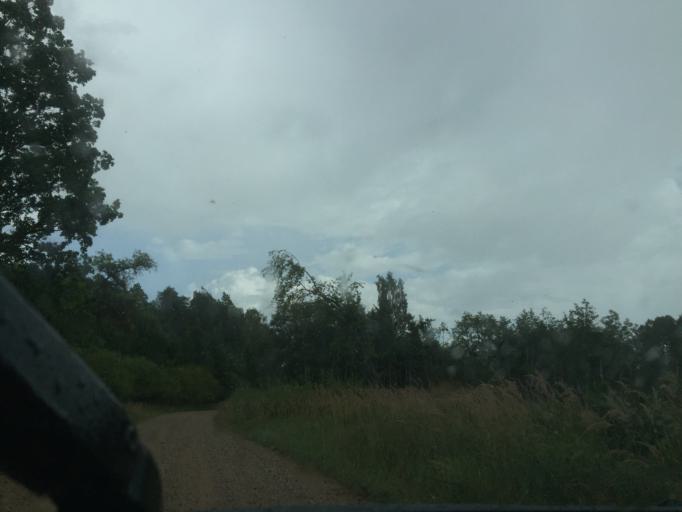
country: LV
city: Tervete
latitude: 56.3731
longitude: 23.4595
